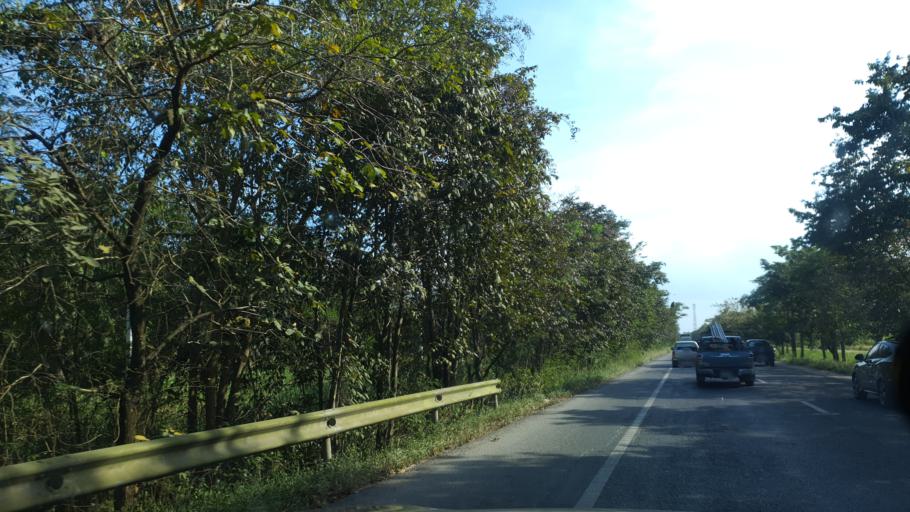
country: TH
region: Surat Thani
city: Ban Na Doem
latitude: 8.9802
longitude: 99.2240
